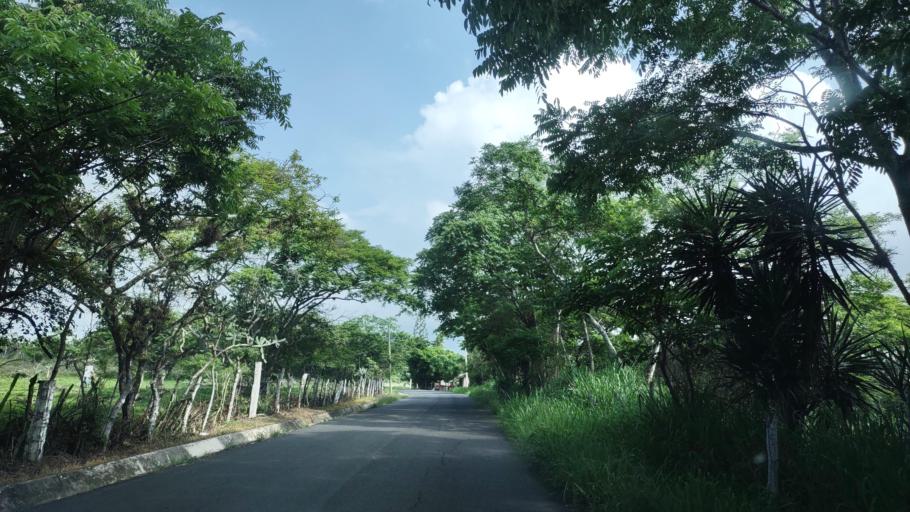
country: MX
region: Veracruz
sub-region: Coatepec
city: Bella Esperanza
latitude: 19.4514
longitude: -96.8279
